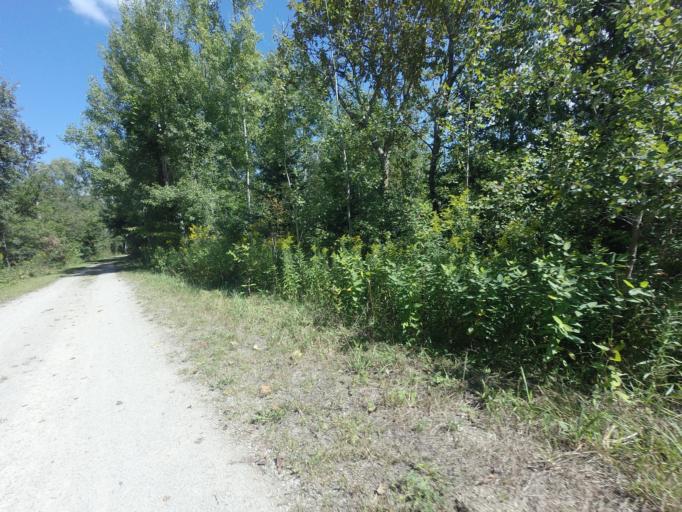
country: CA
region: Ontario
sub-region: Wellington County
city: Guelph
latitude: 43.7639
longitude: -80.3254
